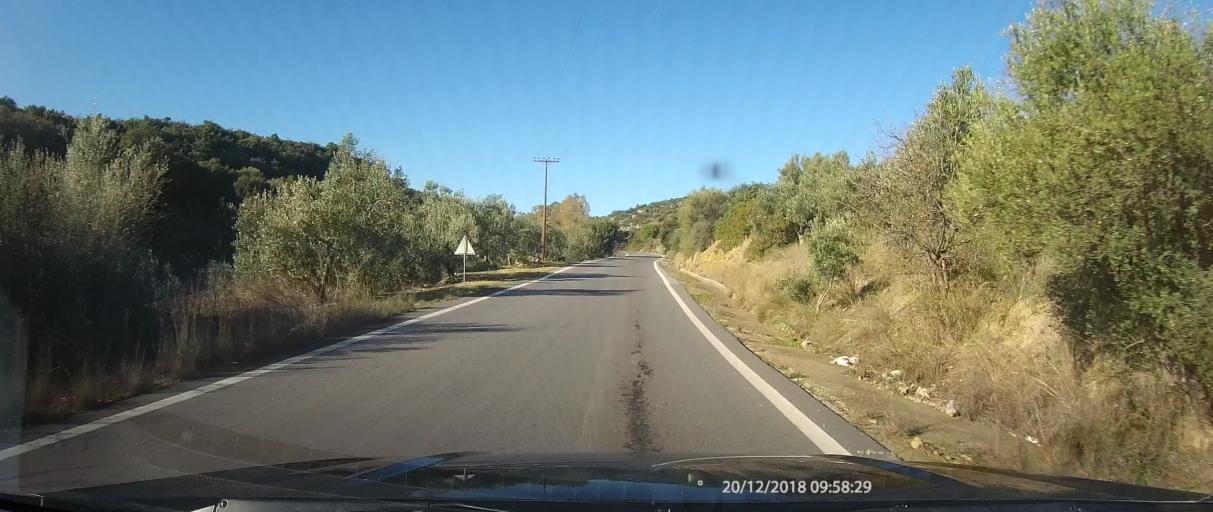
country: GR
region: Peloponnese
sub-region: Nomos Lakonias
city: Yerakion
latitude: 37.0209
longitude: 22.5838
